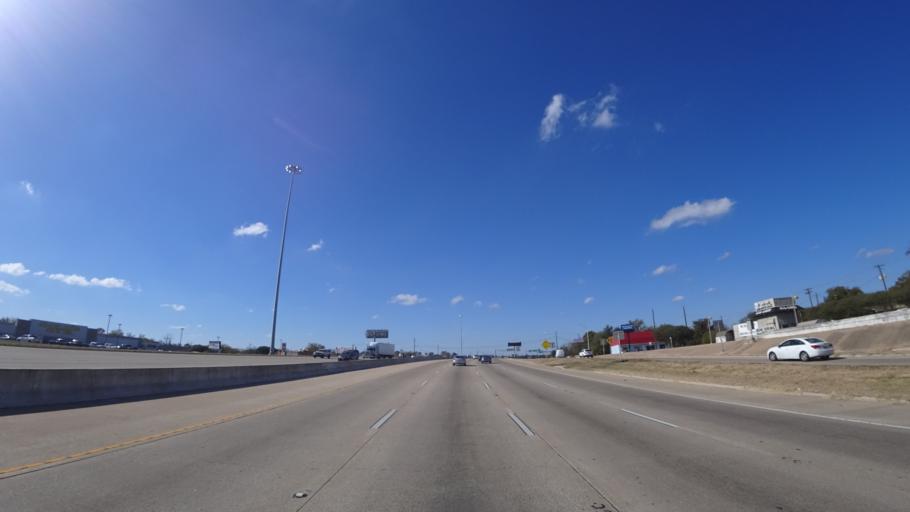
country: US
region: Texas
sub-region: Travis County
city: Rollingwood
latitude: 30.2281
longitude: -97.7832
